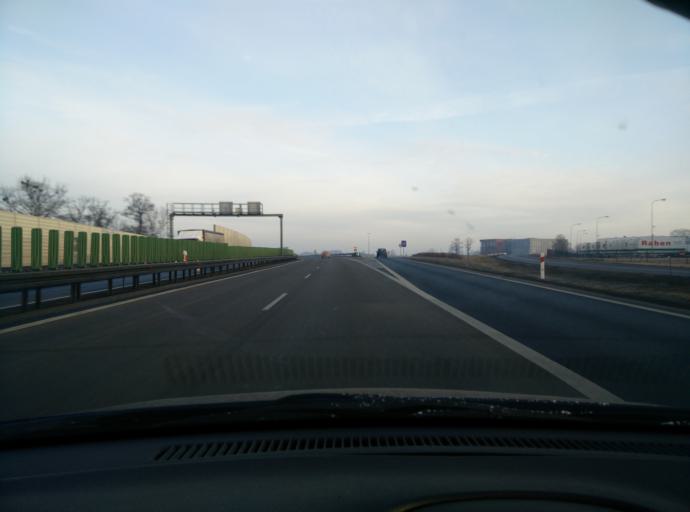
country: PL
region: Greater Poland Voivodeship
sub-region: Powiat poznanski
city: Kornik
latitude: 52.3085
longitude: 17.0470
